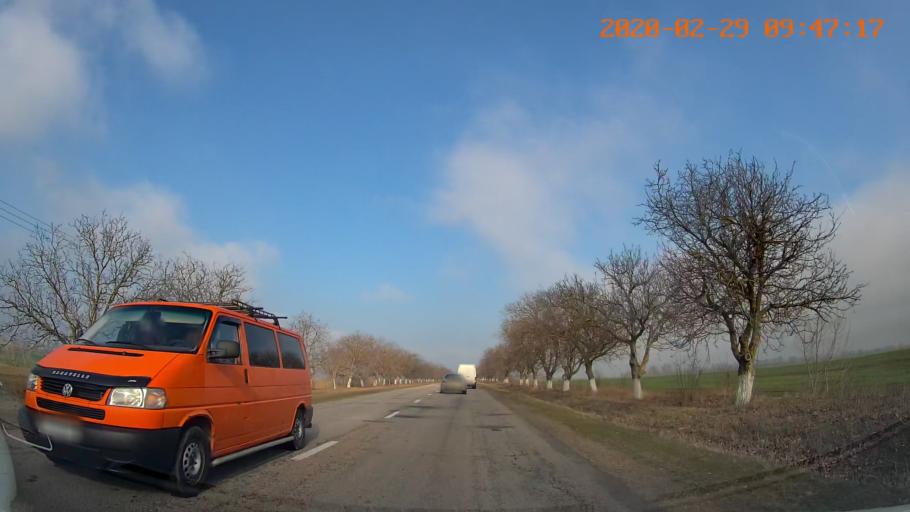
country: MD
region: Telenesti
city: Crasnoe
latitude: 46.6758
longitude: 29.7917
